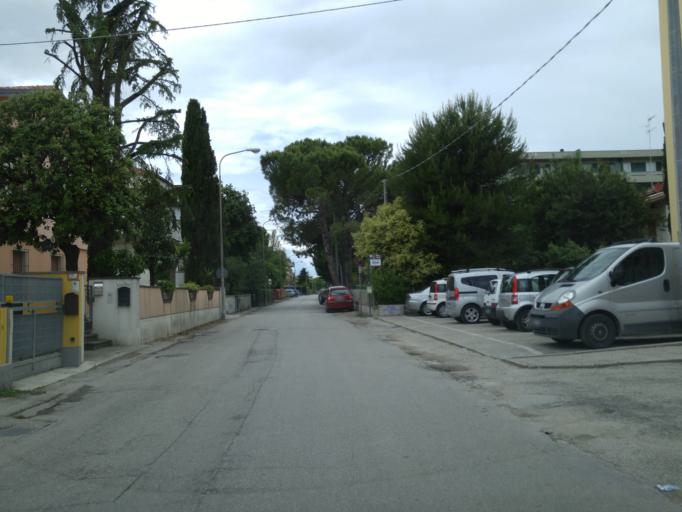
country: IT
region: The Marches
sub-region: Provincia di Pesaro e Urbino
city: Fano
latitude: 43.8330
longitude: 13.0286
